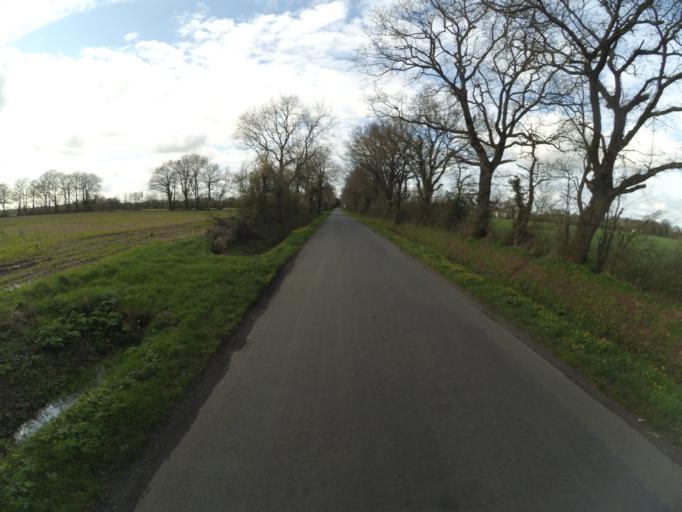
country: FR
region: Pays de la Loire
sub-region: Departement de la Vendee
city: Bouffere
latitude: 46.9693
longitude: -1.3410
